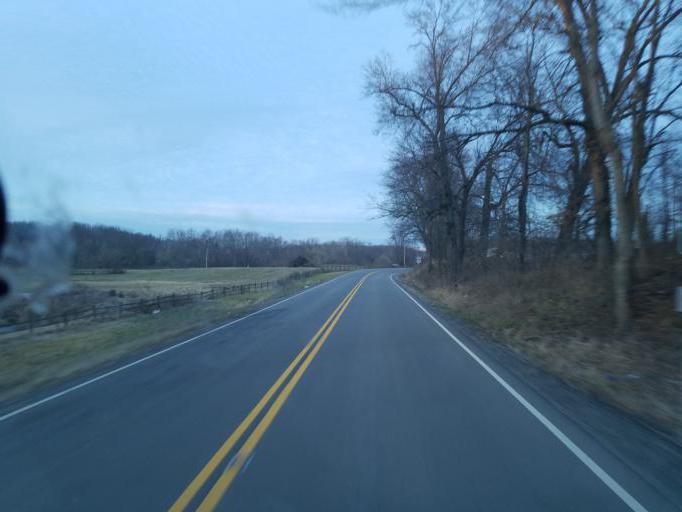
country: US
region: Ohio
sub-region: Muskingum County
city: Dresden
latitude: 40.1608
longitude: -82.0254
